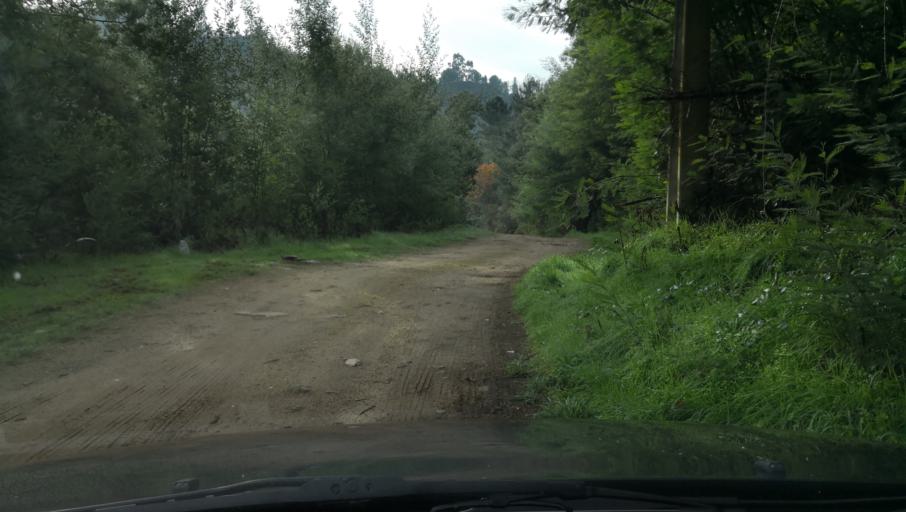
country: PT
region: Vila Real
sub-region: Vila Real
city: Vila Real
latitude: 41.2897
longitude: -7.7492
